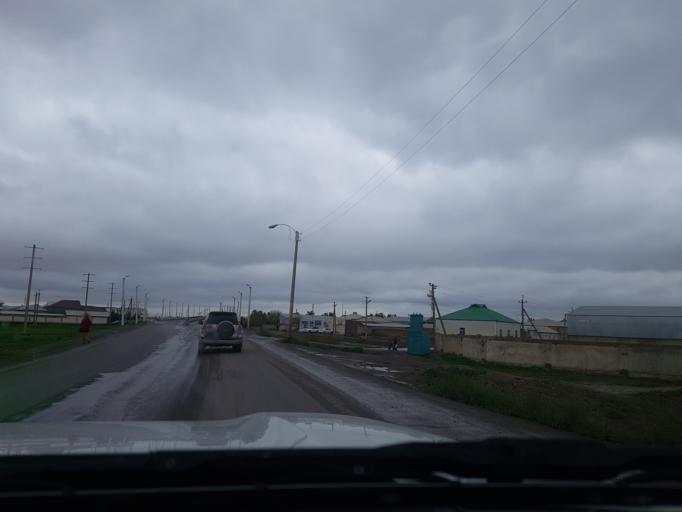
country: TM
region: Mary
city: Mary
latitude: 37.5867
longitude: 61.8818
